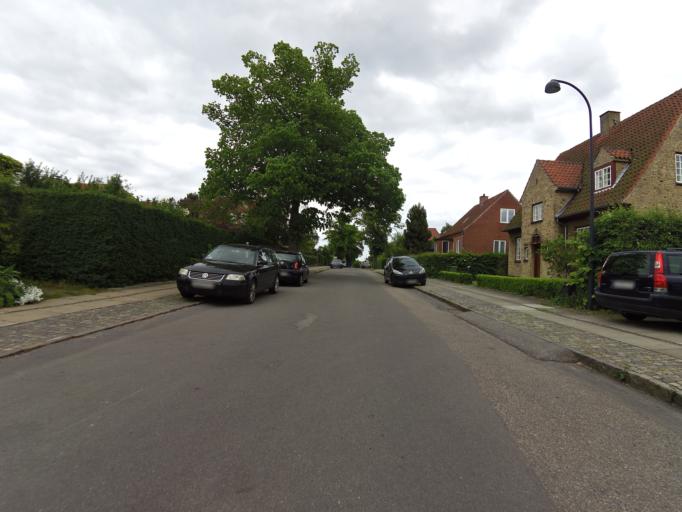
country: DK
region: Capital Region
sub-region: Frederiksberg Kommune
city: Frederiksberg
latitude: 55.7292
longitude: 12.5447
